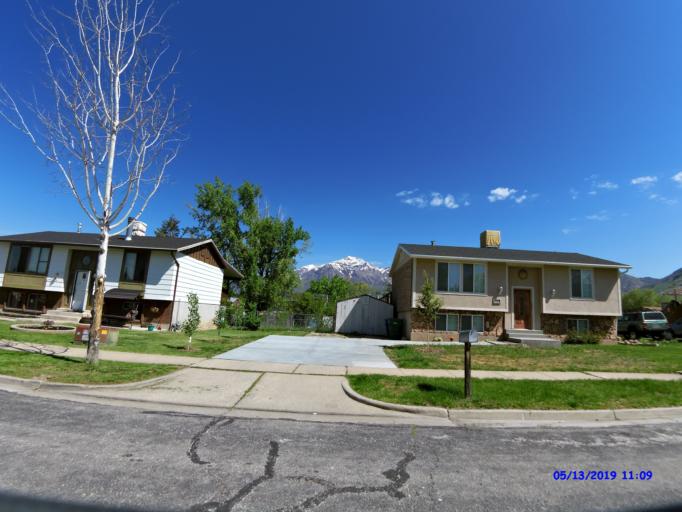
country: US
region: Utah
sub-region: Weber County
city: Harrisville
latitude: 41.2784
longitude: -111.9617
